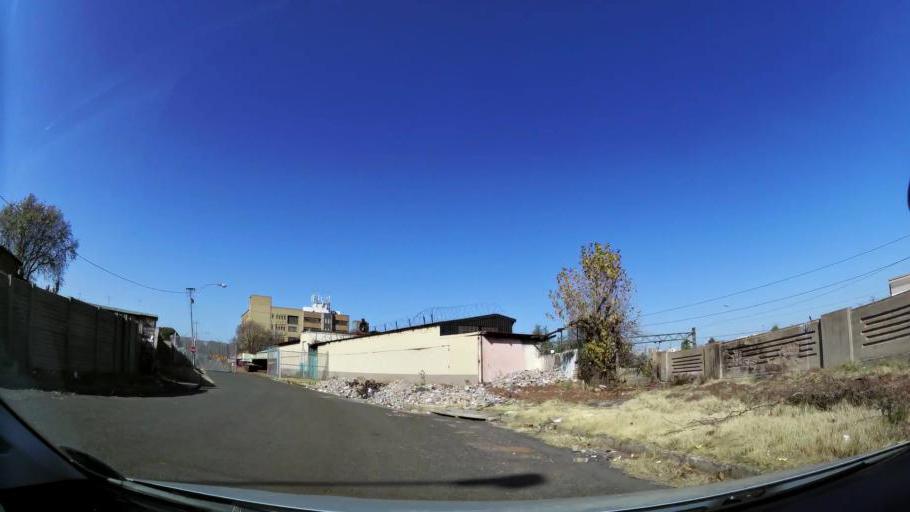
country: ZA
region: Gauteng
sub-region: City of Johannesburg Metropolitan Municipality
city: Johannesburg
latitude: -26.2078
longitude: 28.0696
